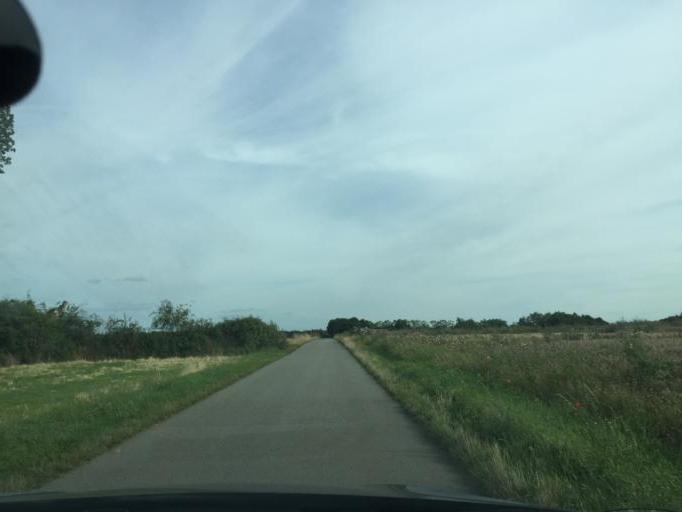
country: DK
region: South Denmark
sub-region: Kerteminde Kommune
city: Langeskov
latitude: 55.3356
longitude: 10.5534
